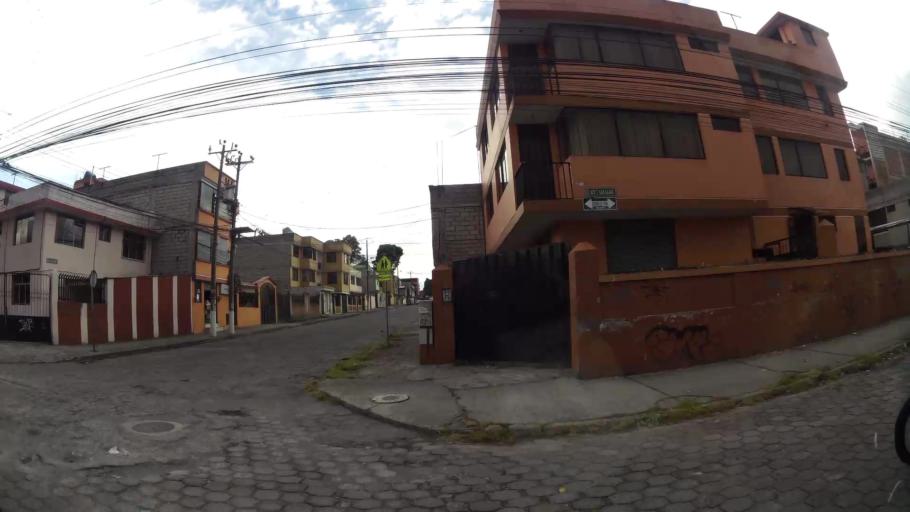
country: EC
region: Pichincha
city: Quito
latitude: -0.2825
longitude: -78.5382
